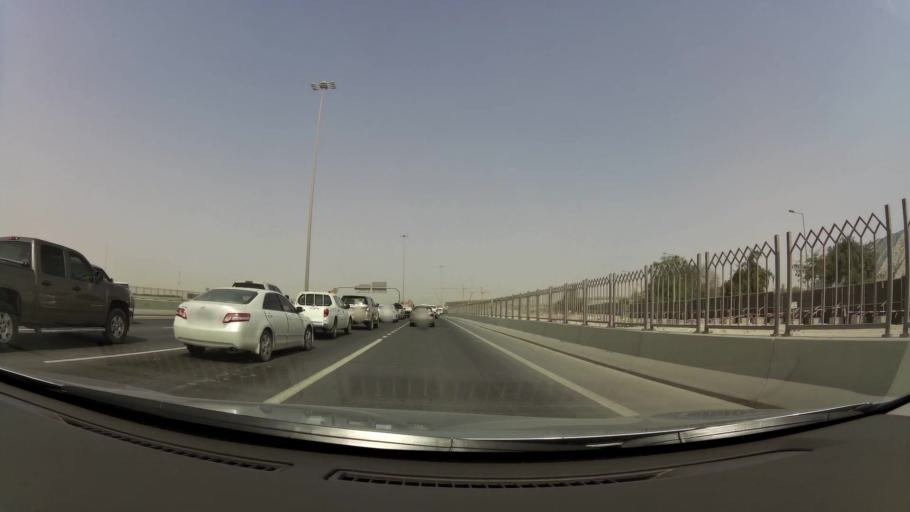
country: QA
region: Baladiyat ad Dawhah
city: Doha
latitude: 25.2892
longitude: 51.4790
